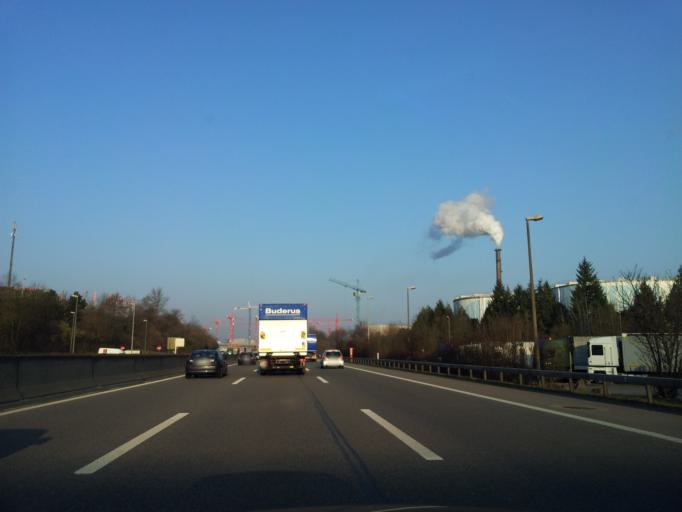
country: CH
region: Basel-Landschaft
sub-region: Bezirk Liestal
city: Pratteln
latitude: 47.5276
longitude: 7.7002
